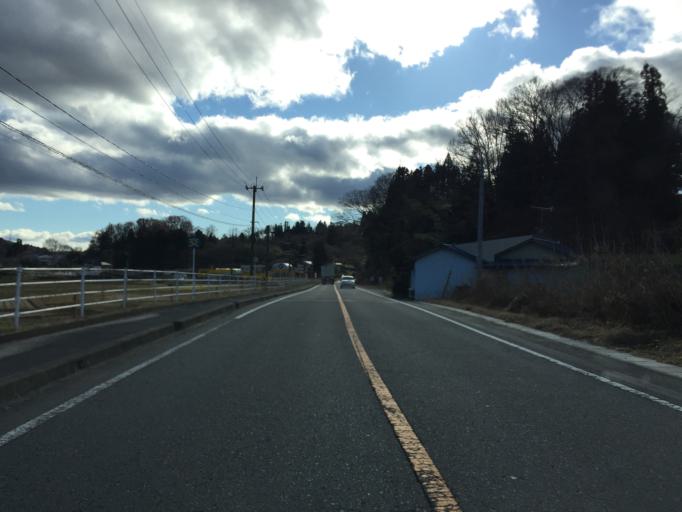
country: JP
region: Fukushima
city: Funehikimachi-funehiki
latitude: 37.5888
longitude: 140.5775
